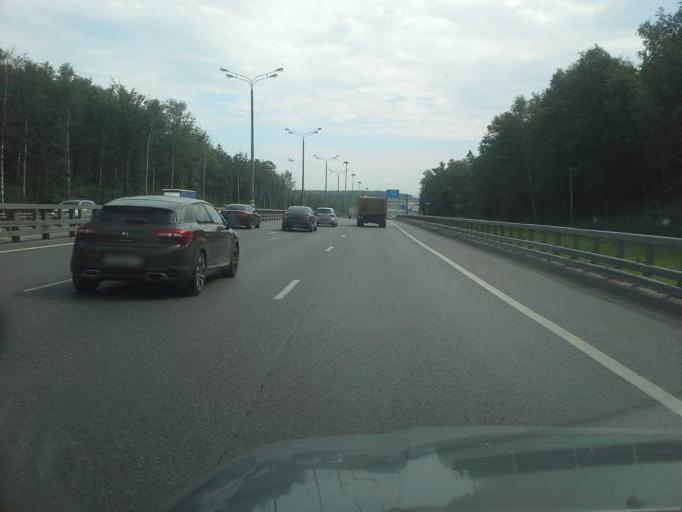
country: RU
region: Moskovskaya
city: Kokoshkino
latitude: 55.5679
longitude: 37.1891
